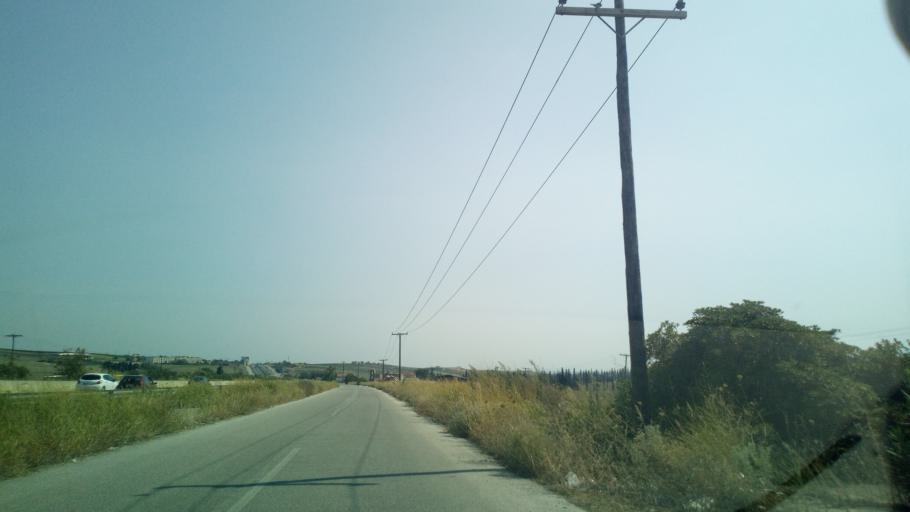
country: GR
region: Central Macedonia
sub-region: Nomos Chalkidikis
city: Lakkoma
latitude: 40.3680
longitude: 23.0463
